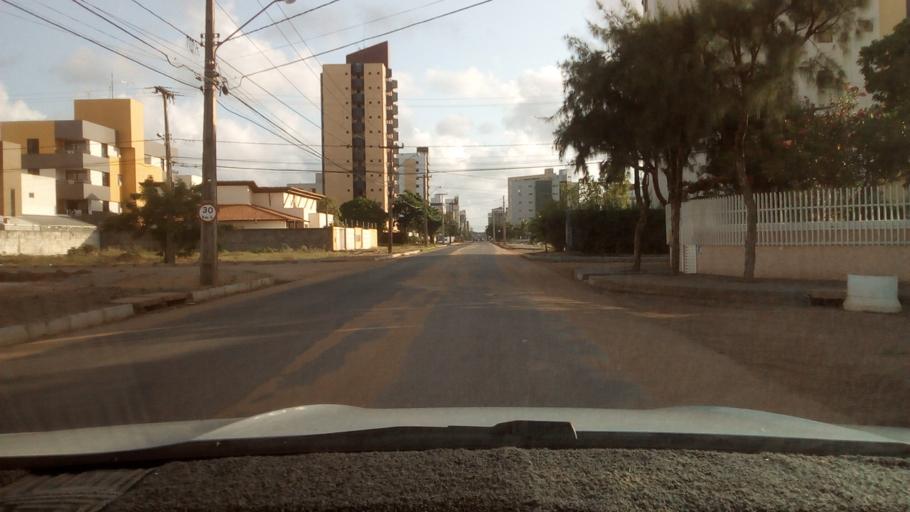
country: BR
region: Paraiba
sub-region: Cabedelo
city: Cabedelo
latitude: -7.0381
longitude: -34.8420
